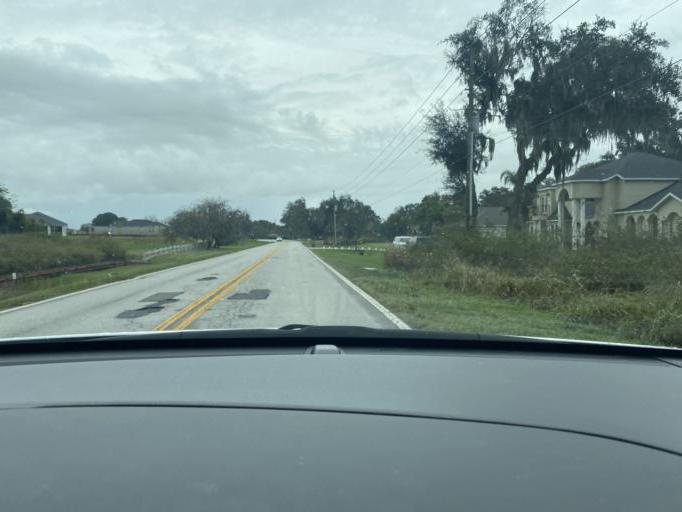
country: US
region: Florida
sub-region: Lake County
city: Clermont
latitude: 28.5834
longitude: -81.7839
